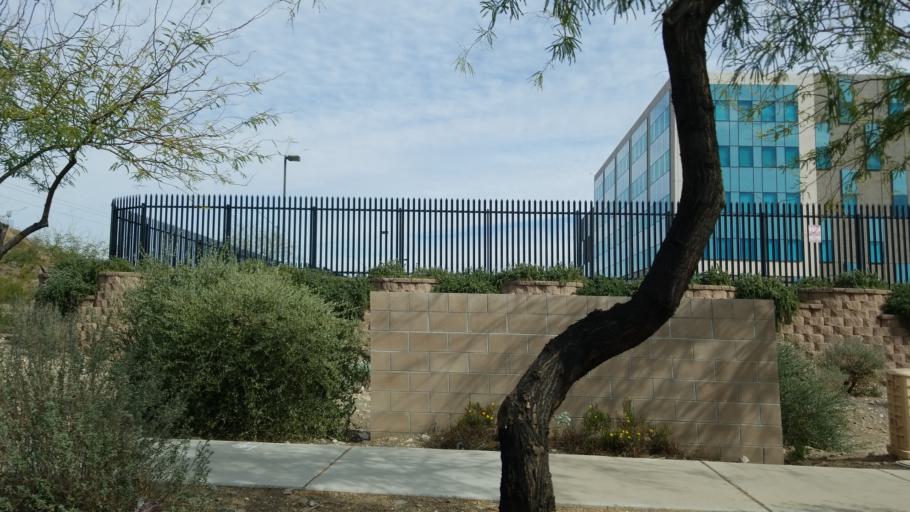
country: US
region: Arizona
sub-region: Maricopa County
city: Glendale
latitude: 33.6826
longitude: -112.0654
